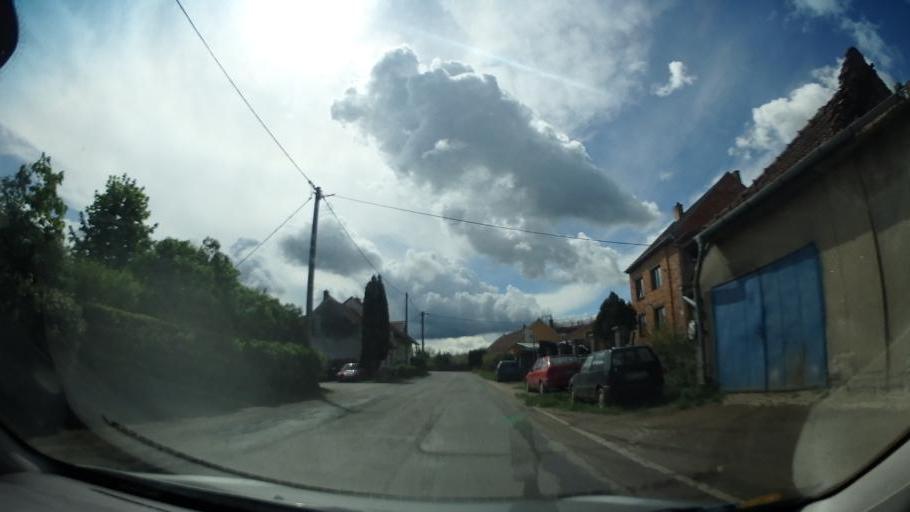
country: CZ
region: South Moravian
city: Ricany
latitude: 49.2351
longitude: 16.4055
